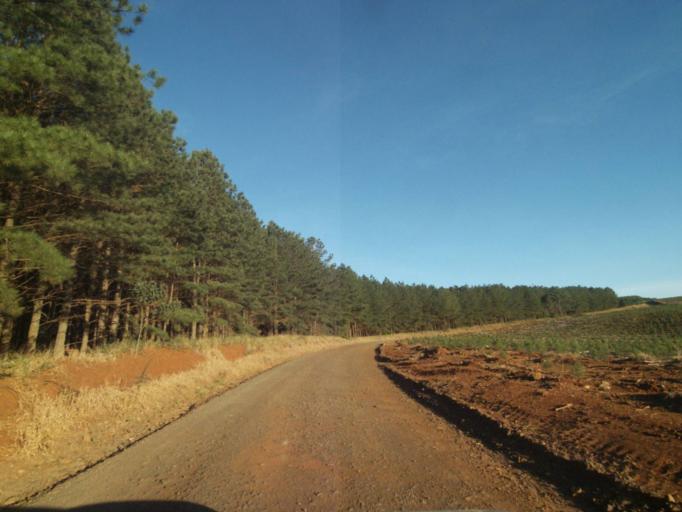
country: BR
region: Parana
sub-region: Telemaco Borba
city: Telemaco Borba
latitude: -24.4469
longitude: -50.5979
